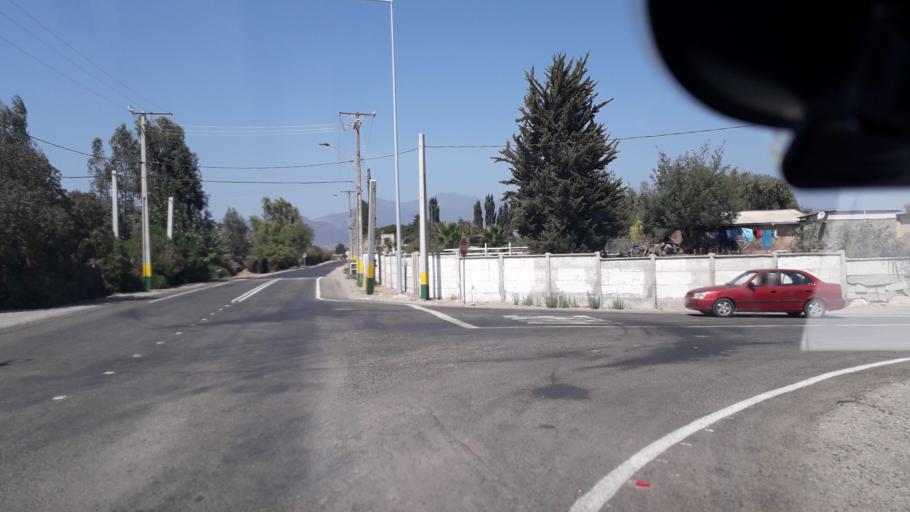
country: CL
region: Valparaiso
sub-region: Provincia de Quillota
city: Hacienda La Calera
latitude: -32.8179
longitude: -71.2398
